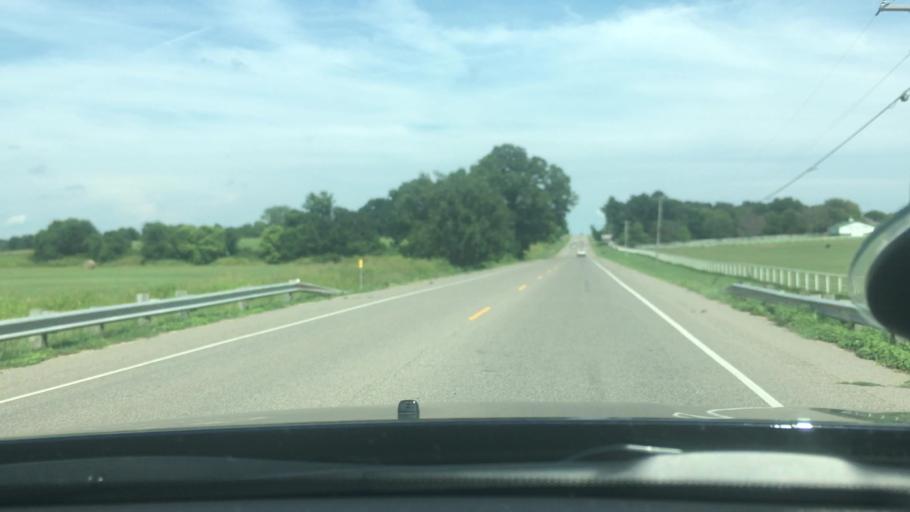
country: US
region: Oklahoma
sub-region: Pottawatomie County
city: Shawnee
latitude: 35.3331
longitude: -96.8313
